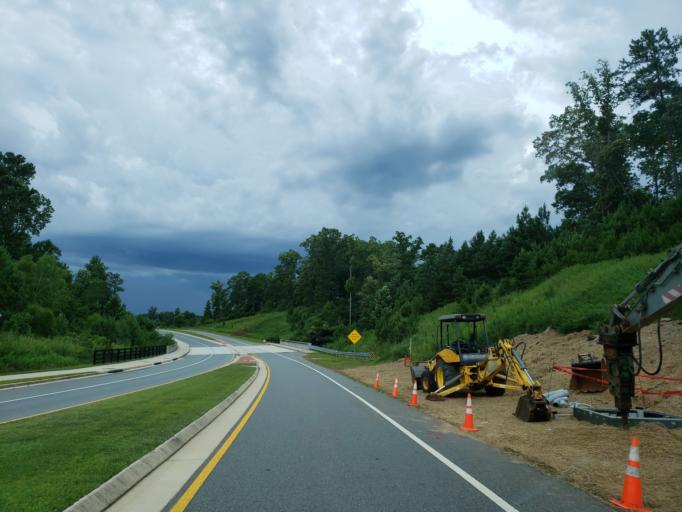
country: US
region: Georgia
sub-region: Cobb County
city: Acworth
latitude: 34.0299
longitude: -84.7611
